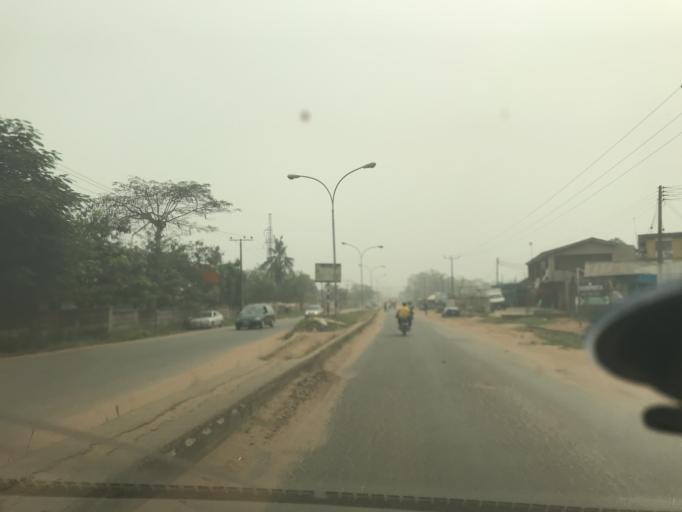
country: NG
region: Ogun
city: Shagamu
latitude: 6.8531
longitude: 3.6309
